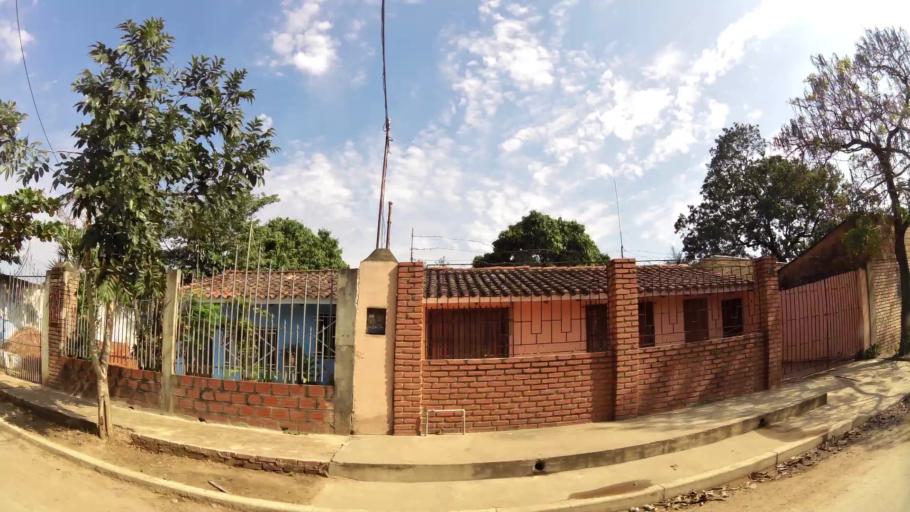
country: BO
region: Santa Cruz
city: Santa Cruz de la Sierra
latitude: -17.7311
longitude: -63.1486
